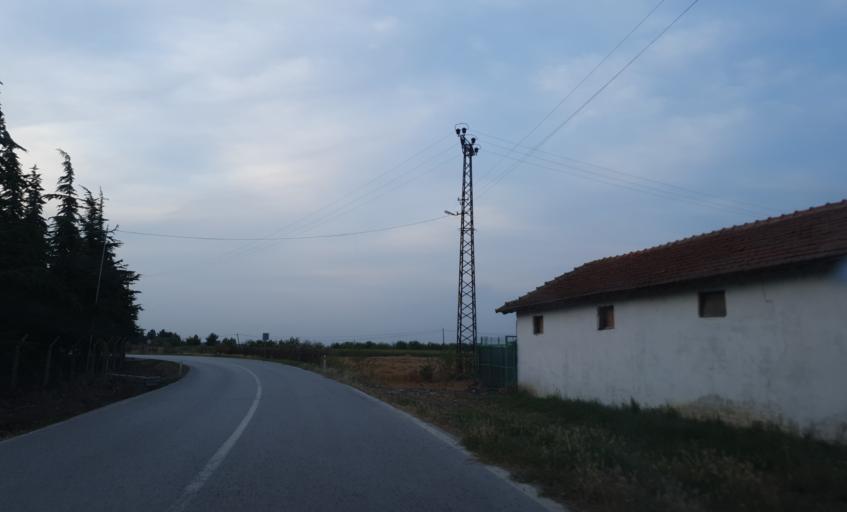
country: TR
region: Kirklareli
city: Buyukkaristiran
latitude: 41.3491
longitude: 27.6104
